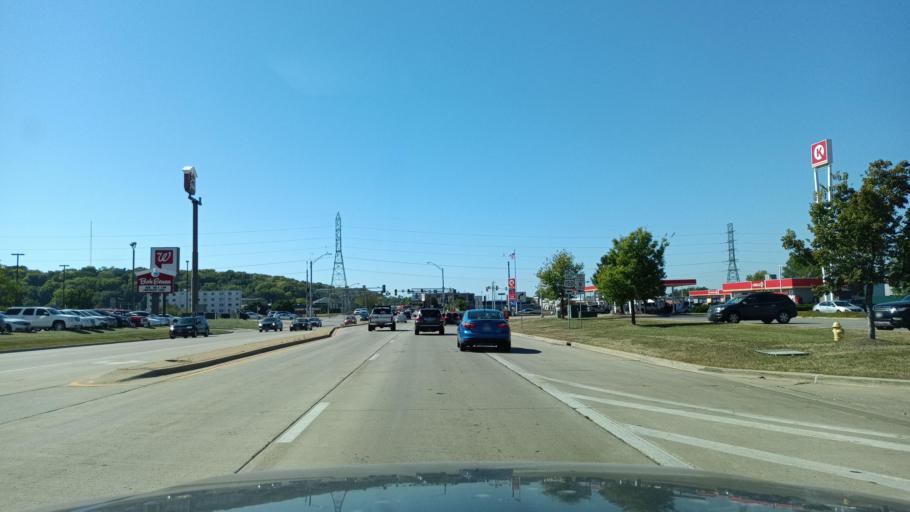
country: US
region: Illinois
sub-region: Tazewell County
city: East Peoria
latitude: 40.6695
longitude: -89.5756
